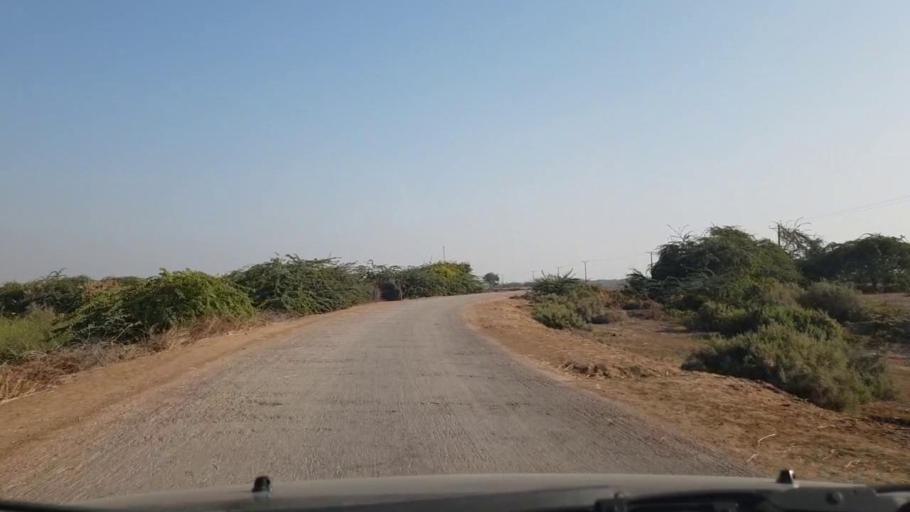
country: PK
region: Sindh
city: Tando Bago
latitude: 24.8492
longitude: 69.0349
